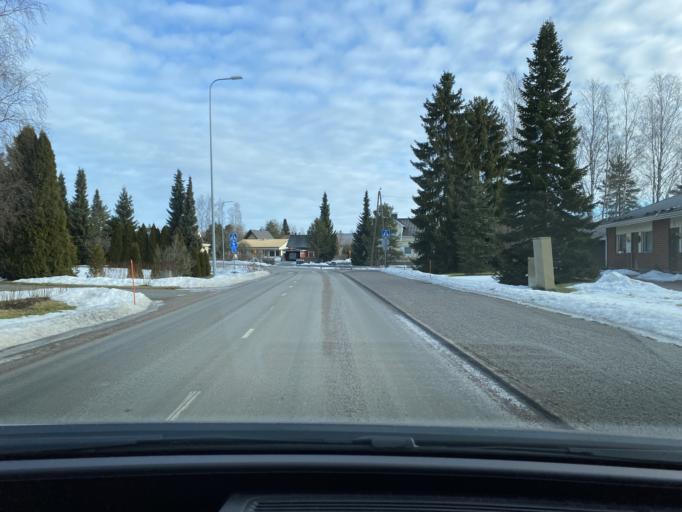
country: FI
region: Satakunta
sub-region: Pori
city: Huittinen
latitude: 61.1709
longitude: 22.6939
